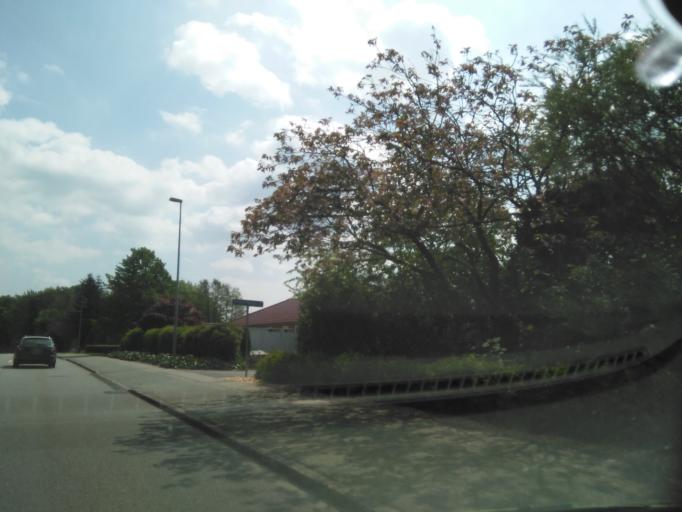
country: DK
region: Central Jutland
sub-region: Skanderborg Kommune
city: Skanderborg
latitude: 56.0354
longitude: 9.9489
